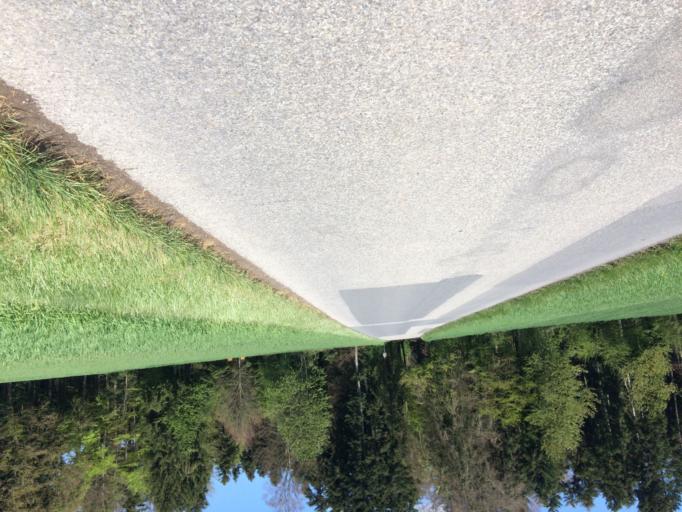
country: CH
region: Bern
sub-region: Bern-Mittelland District
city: Rubigen
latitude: 46.9226
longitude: 7.5391
